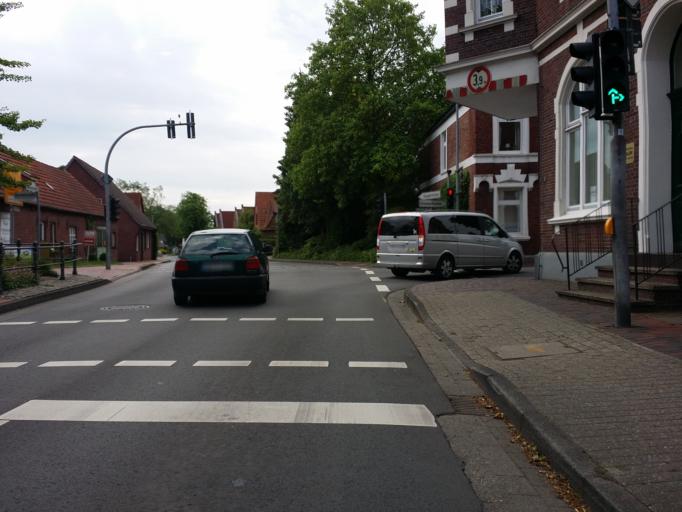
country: DE
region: Lower Saxony
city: Wittmund
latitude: 53.5761
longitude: 7.7799
